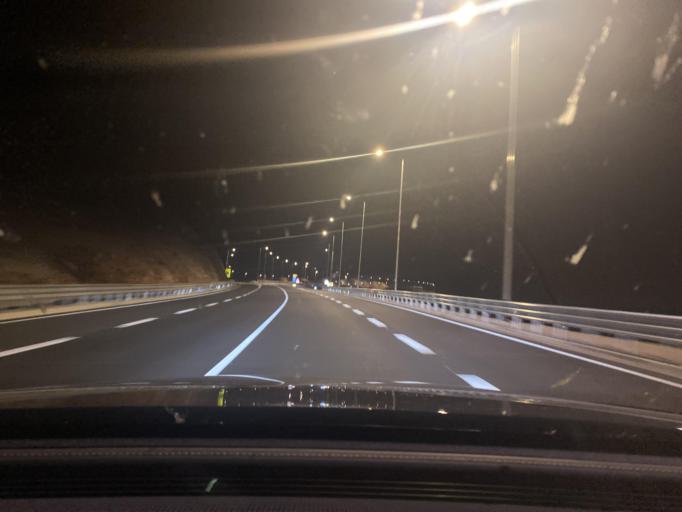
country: BA
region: Federation of Bosnia and Herzegovina
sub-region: Hercegovacko-Bosanski Kanton
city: Neum
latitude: 42.9086
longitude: 17.5334
